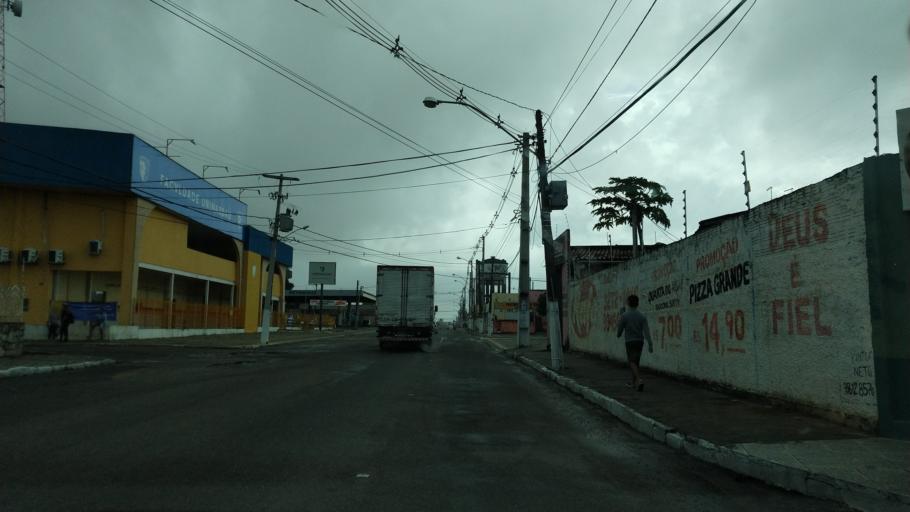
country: BR
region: Rio Grande do Norte
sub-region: Parnamirim
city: Parnamirim
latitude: -5.9223
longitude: -35.2699
